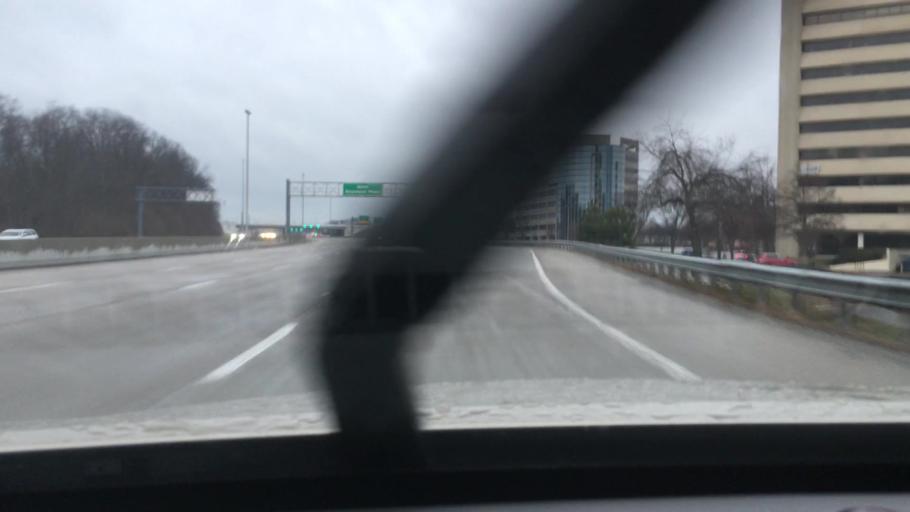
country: US
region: Indiana
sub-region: Marion County
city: Meridian Hills
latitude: 39.9162
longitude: -86.1124
